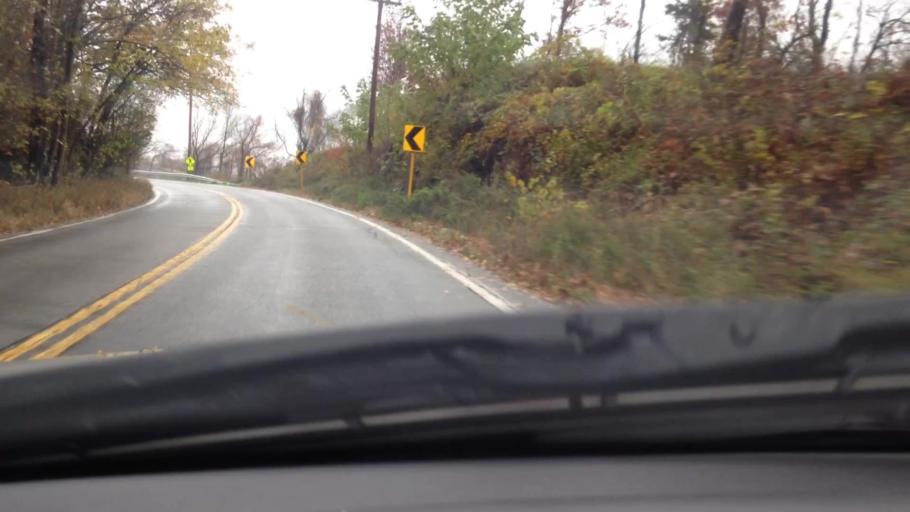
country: US
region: New York
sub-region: Orange County
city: Cornwall-on-Hudson
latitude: 41.4515
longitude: -73.9827
